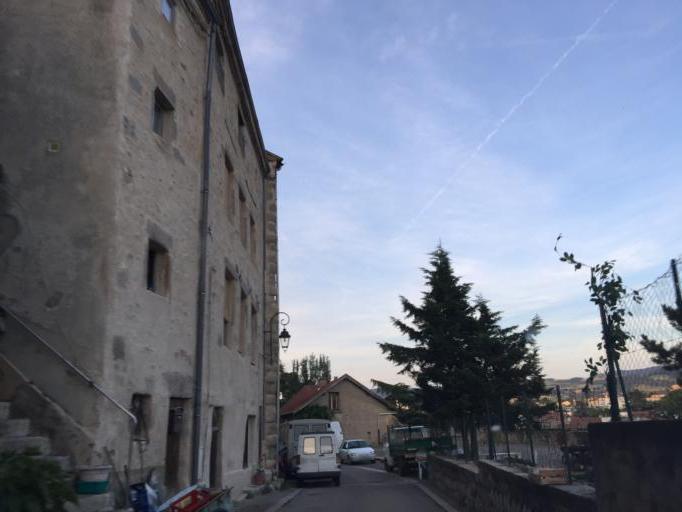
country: FR
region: Rhone-Alpes
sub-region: Departement de la Loire
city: Saint-Chamond
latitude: 45.4782
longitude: 4.5092
